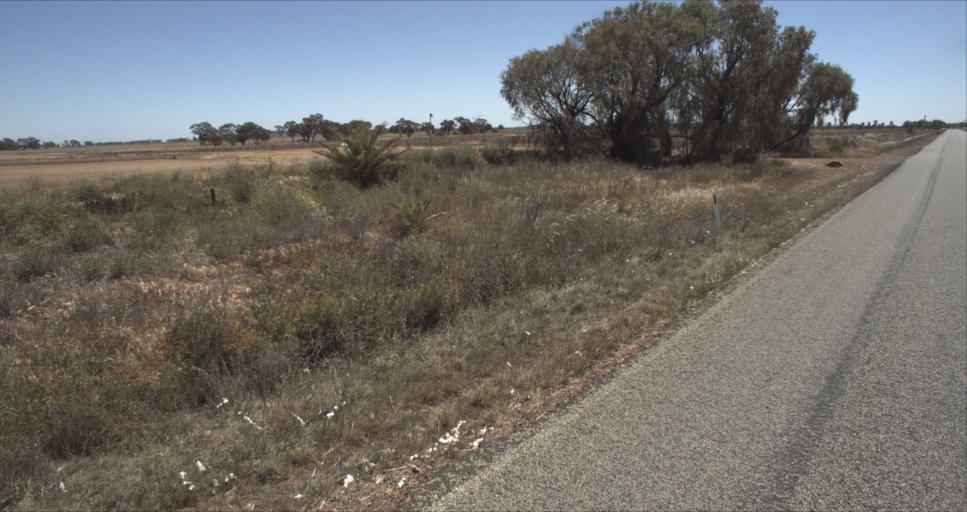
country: AU
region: New South Wales
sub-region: Leeton
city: Leeton
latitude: -34.4494
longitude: 146.2963
